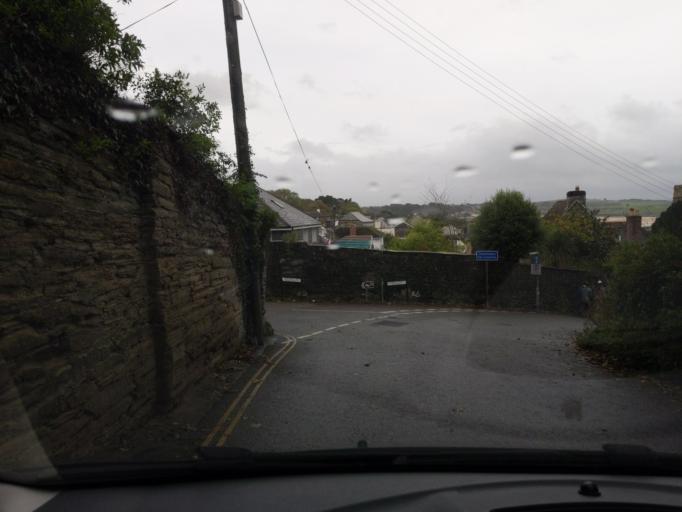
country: GB
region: England
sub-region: Cornwall
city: Padstow
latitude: 50.5413
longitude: -4.9450
